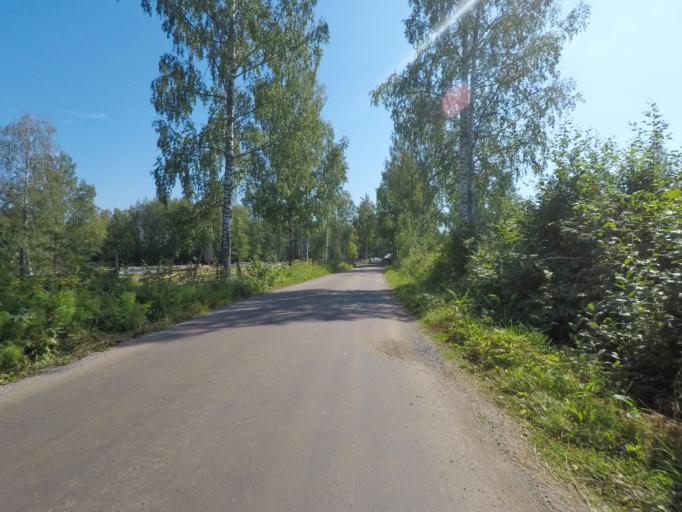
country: FI
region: Southern Savonia
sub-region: Mikkeli
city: Puumala
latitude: 61.4275
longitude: 28.0292
